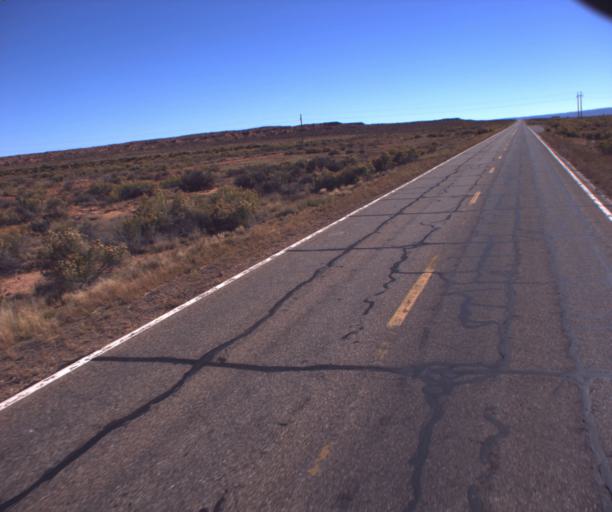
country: US
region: Arizona
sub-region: Coconino County
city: Fredonia
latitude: 36.9352
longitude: -112.5074
